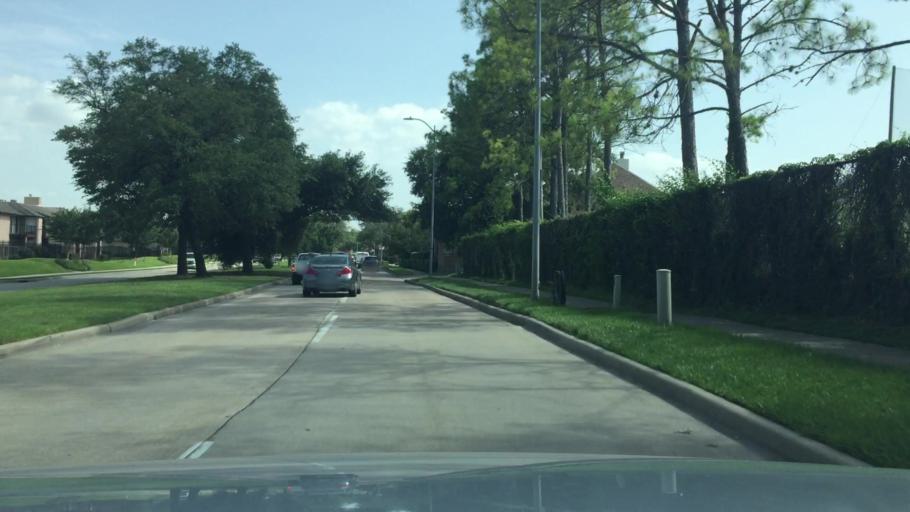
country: US
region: Texas
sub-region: Harris County
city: Bunker Hill Village
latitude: 29.7604
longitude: -95.5765
